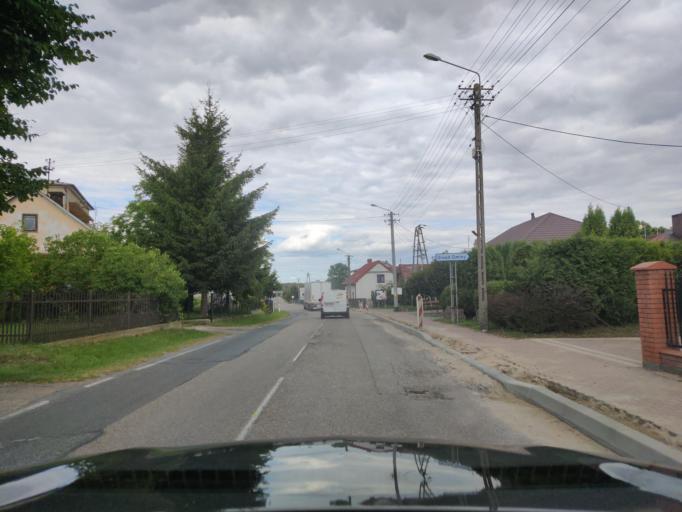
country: PL
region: Masovian Voivodeship
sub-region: Powiat sokolowski
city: Ceranow
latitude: 52.6347
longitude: 22.2313
